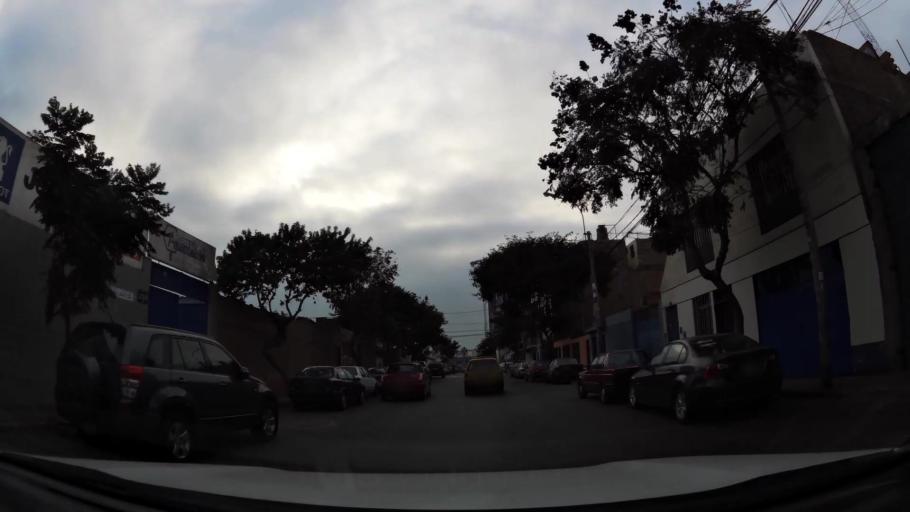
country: PE
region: Lima
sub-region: Lima
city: Surco
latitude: -12.1403
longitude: -77.0156
